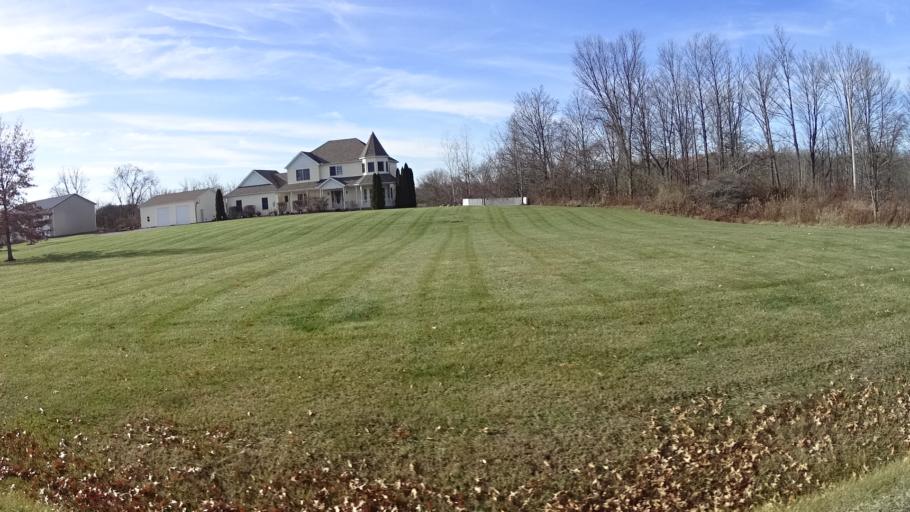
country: US
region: Ohio
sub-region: Lorain County
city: Wellington
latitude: 41.0888
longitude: -82.2400
